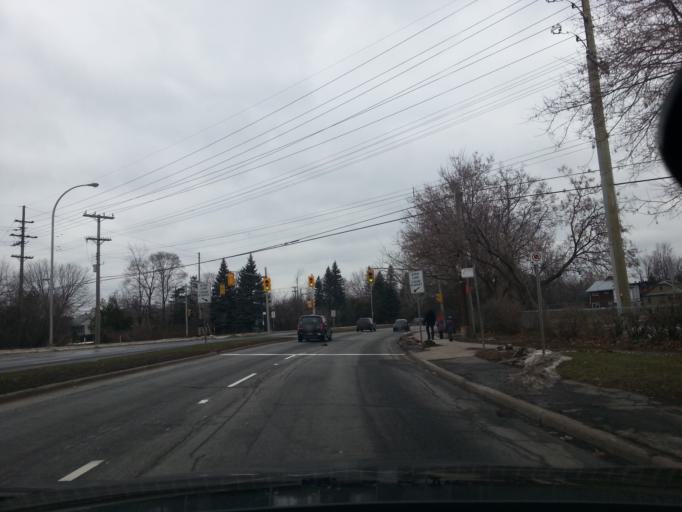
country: CA
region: Ontario
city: Ottawa
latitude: 45.4223
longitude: -75.6606
